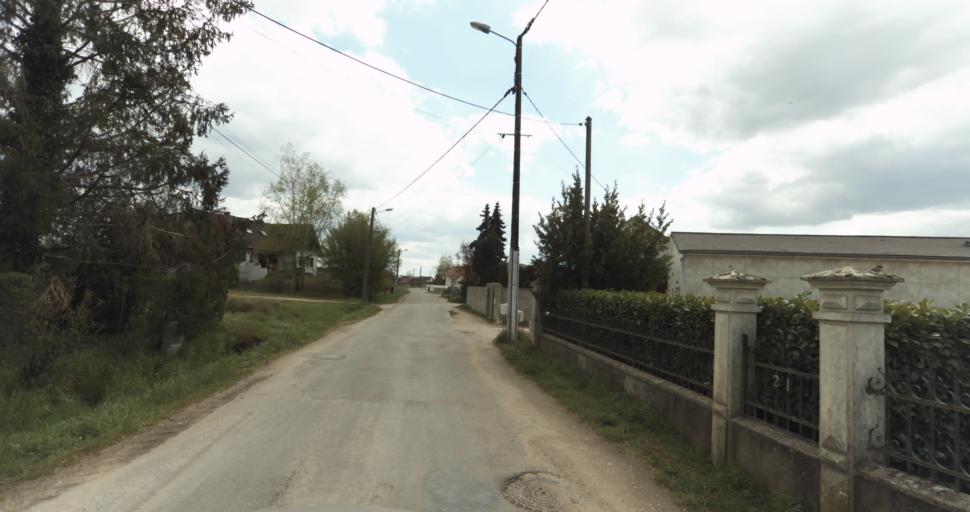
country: FR
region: Bourgogne
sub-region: Departement de la Cote-d'Or
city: Auxonne
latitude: 47.1807
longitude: 5.3924
